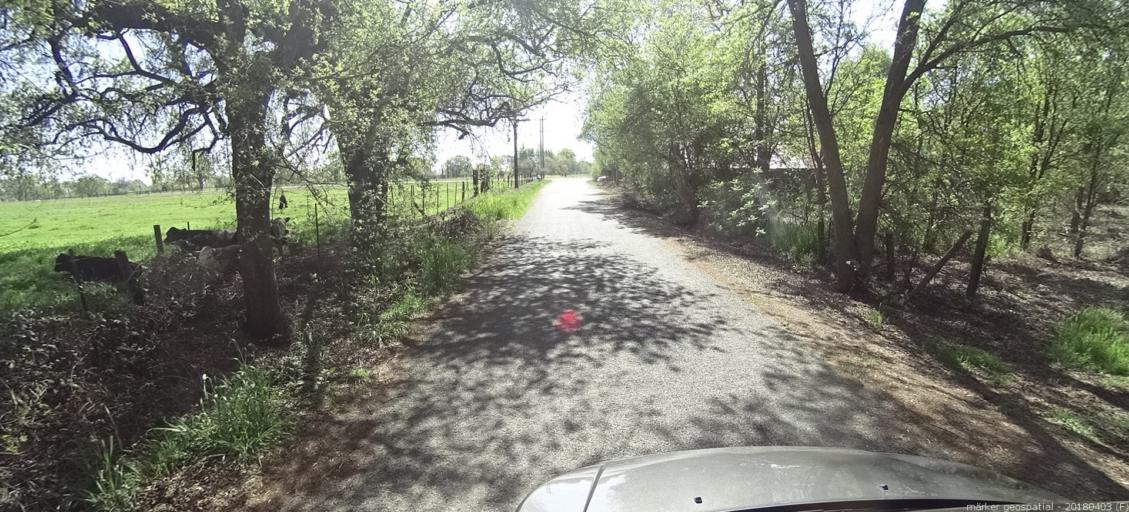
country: US
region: California
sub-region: Sacramento County
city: Wilton
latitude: 38.4294
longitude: -121.2062
